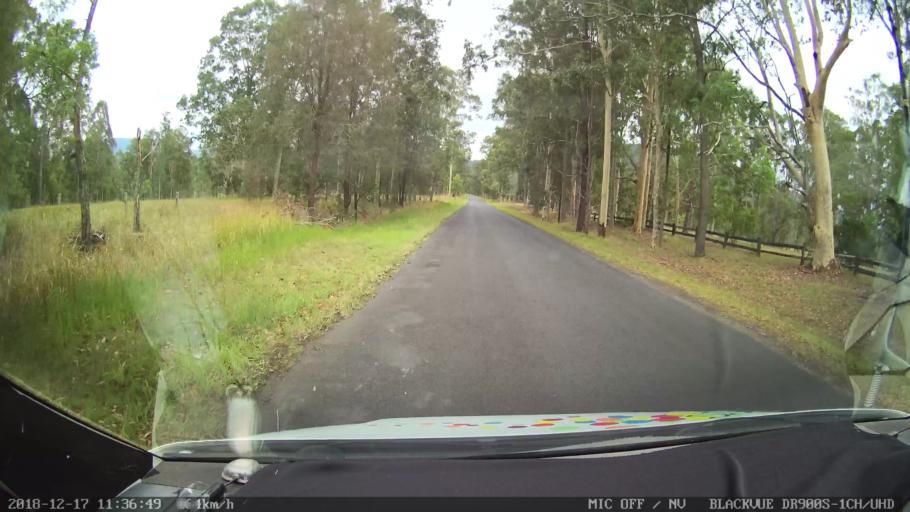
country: AU
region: New South Wales
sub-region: Kyogle
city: Kyogle
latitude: -28.7105
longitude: 152.6062
